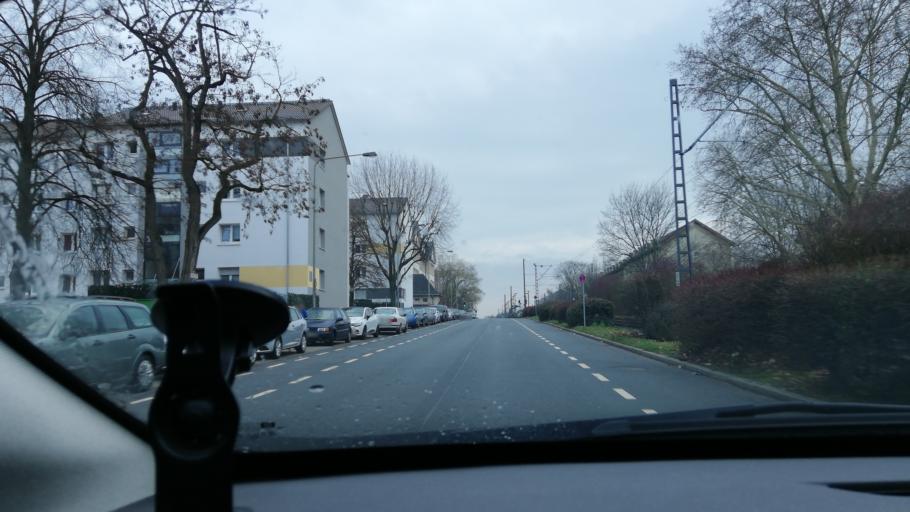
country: DE
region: Hesse
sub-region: Regierungsbezirk Darmstadt
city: Frankfurt am Main
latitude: 50.1495
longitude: 8.6893
